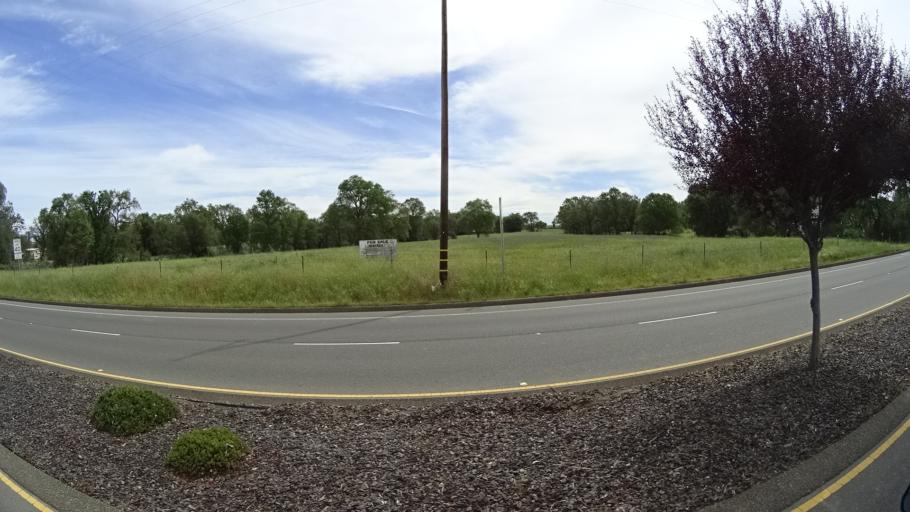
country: US
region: California
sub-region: Placer County
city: Loomis
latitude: 38.8082
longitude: -121.2055
